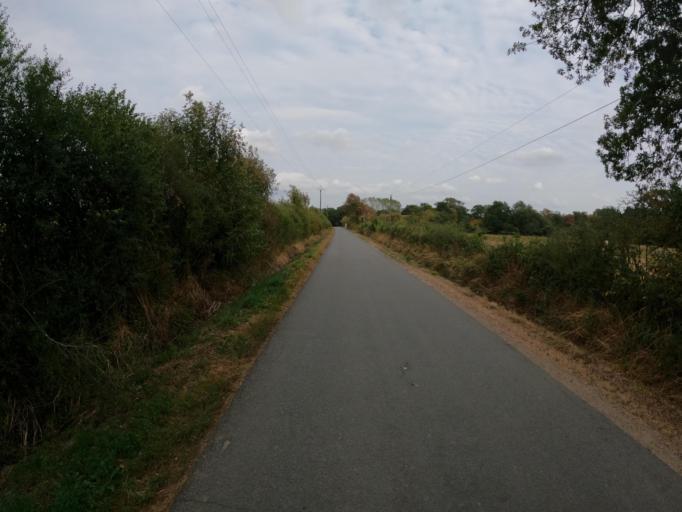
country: FR
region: Pays de la Loire
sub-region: Departement de Maine-et-Loire
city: La Romagne
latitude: 47.0502
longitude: -1.0003
